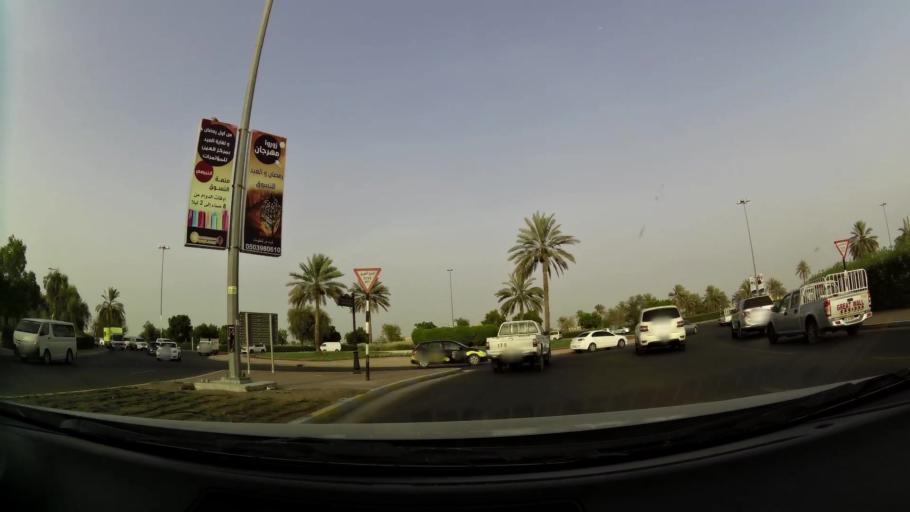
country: OM
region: Al Buraimi
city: Al Buraymi
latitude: 24.2408
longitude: 55.7514
